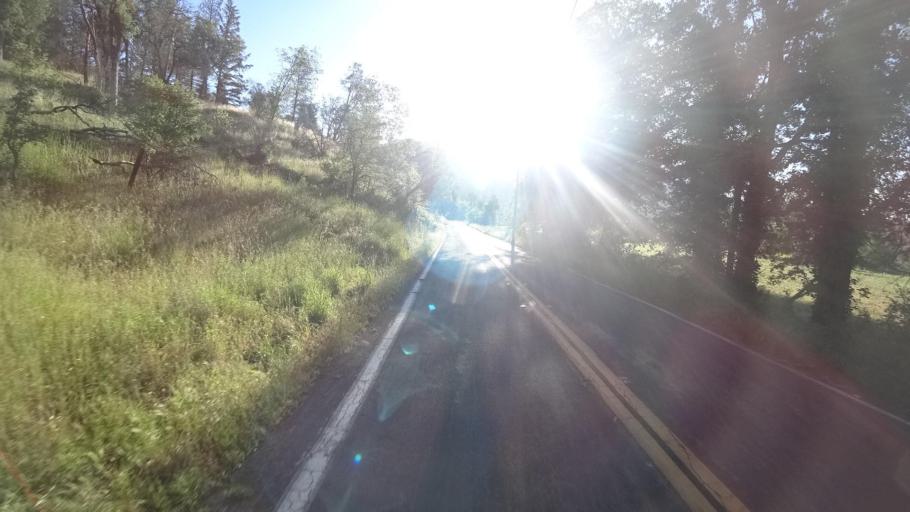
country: US
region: California
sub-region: Lake County
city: Upper Lake
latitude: 39.2083
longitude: -122.9216
